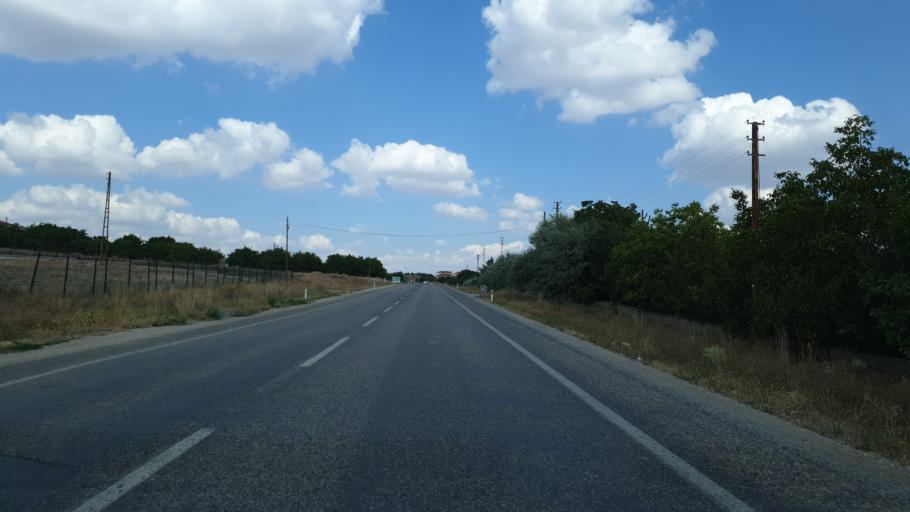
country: TR
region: Kayseri
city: Felahiye
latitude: 39.1035
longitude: 35.5927
